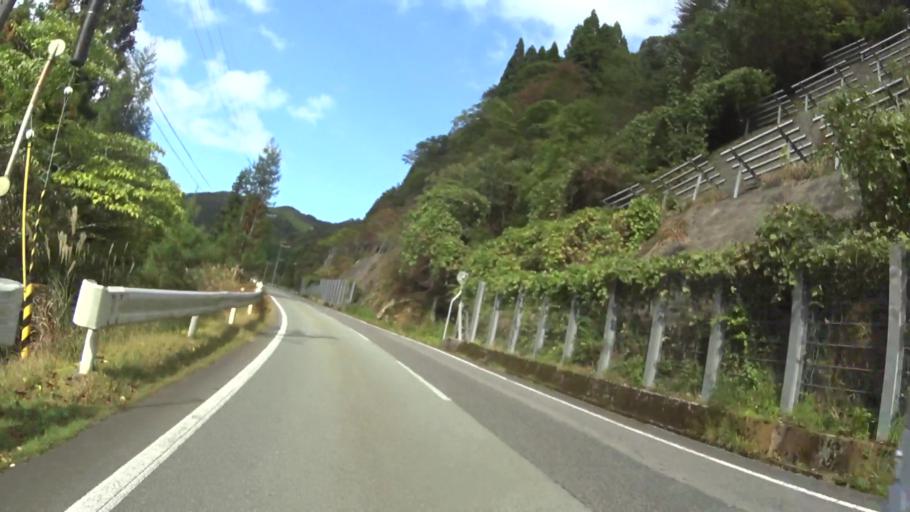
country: JP
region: Hyogo
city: Toyooka
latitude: 35.5166
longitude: 134.9903
